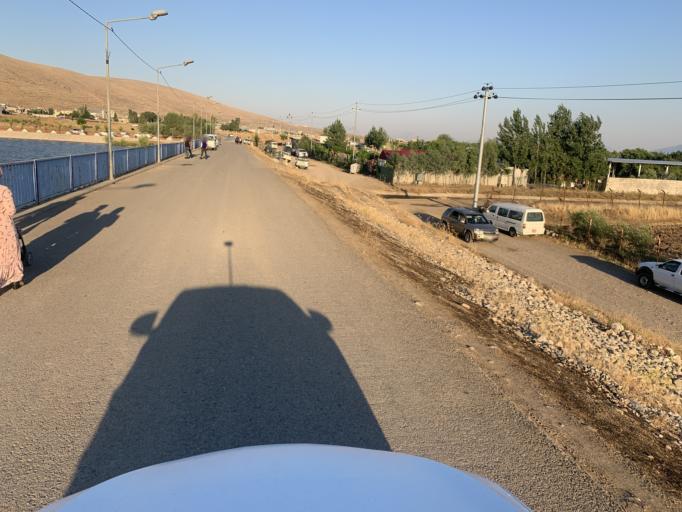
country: IQ
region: As Sulaymaniyah
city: Raniye
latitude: 36.2720
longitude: 44.7534
